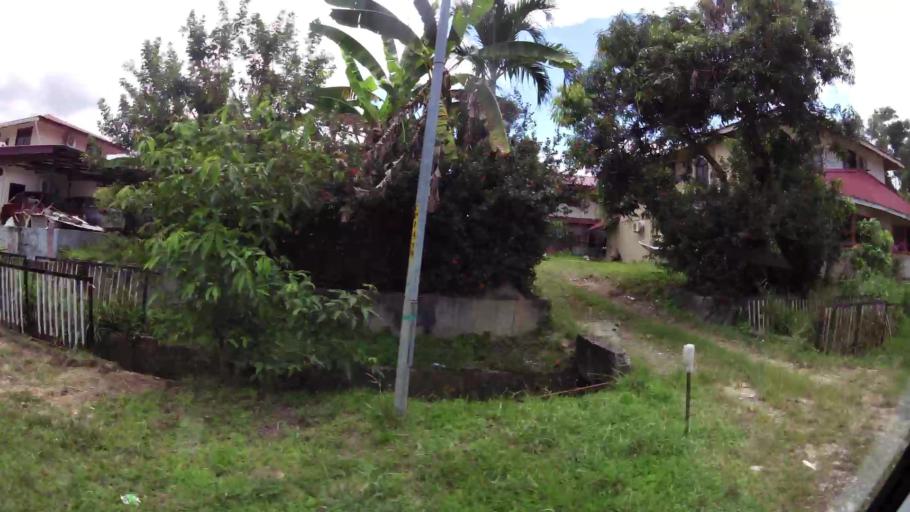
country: BN
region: Brunei and Muara
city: Bandar Seri Begawan
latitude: 4.9835
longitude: 114.9372
